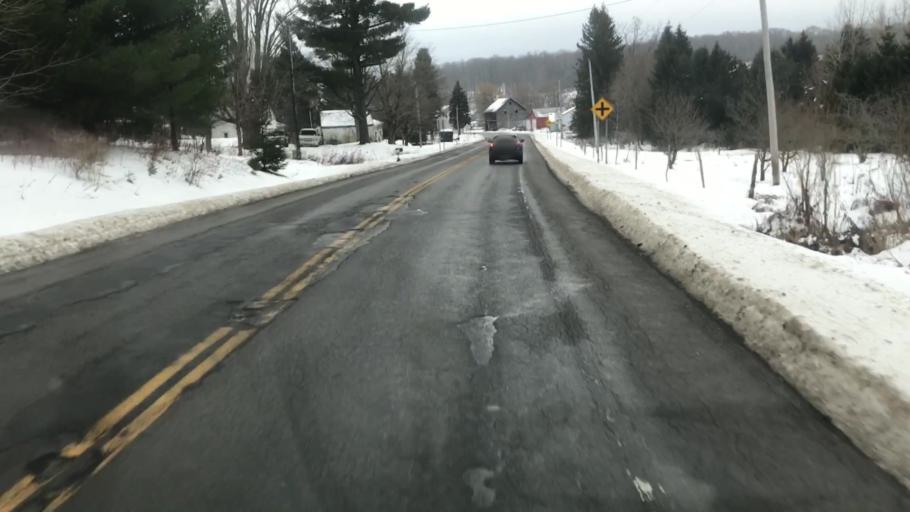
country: US
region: New York
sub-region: Cayuga County
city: Moravia
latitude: 42.7314
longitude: -76.3141
